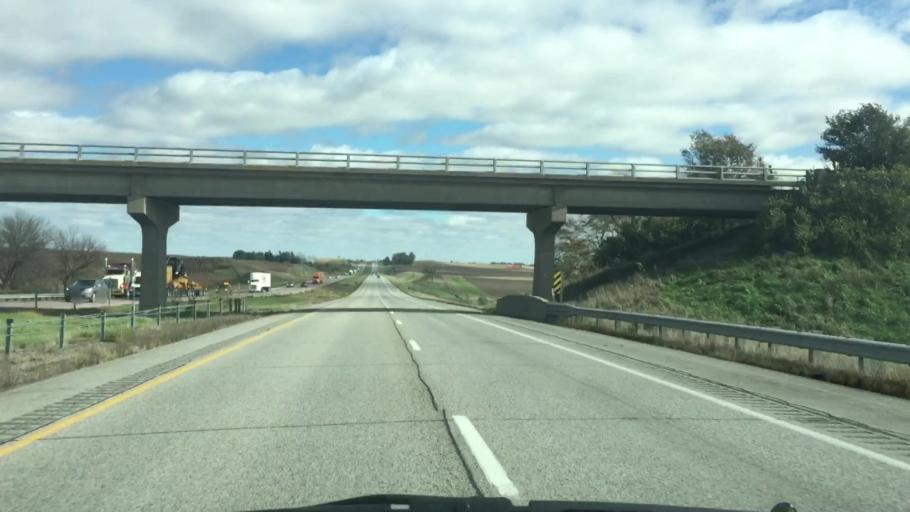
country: US
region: Iowa
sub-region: Iowa County
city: Marengo
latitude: 41.6939
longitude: -92.1244
